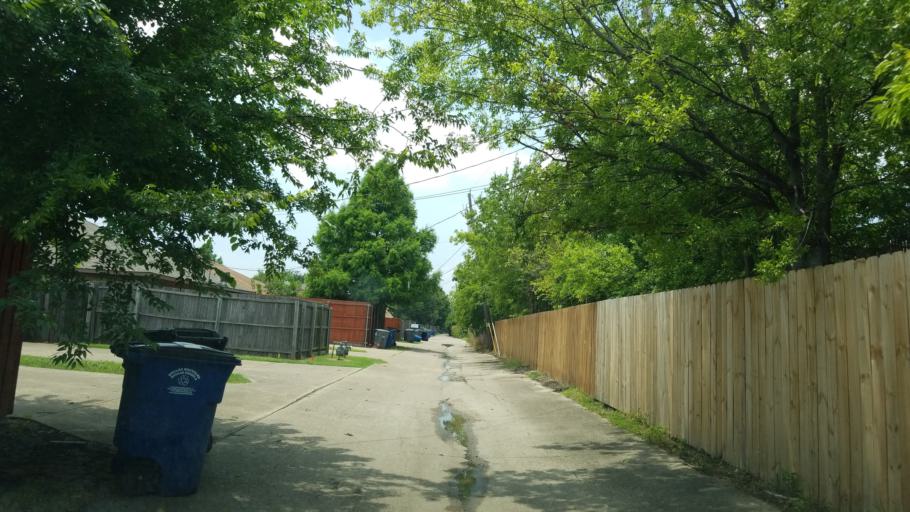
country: US
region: Texas
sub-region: Dallas County
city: Farmers Branch
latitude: 32.9082
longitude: -96.8748
